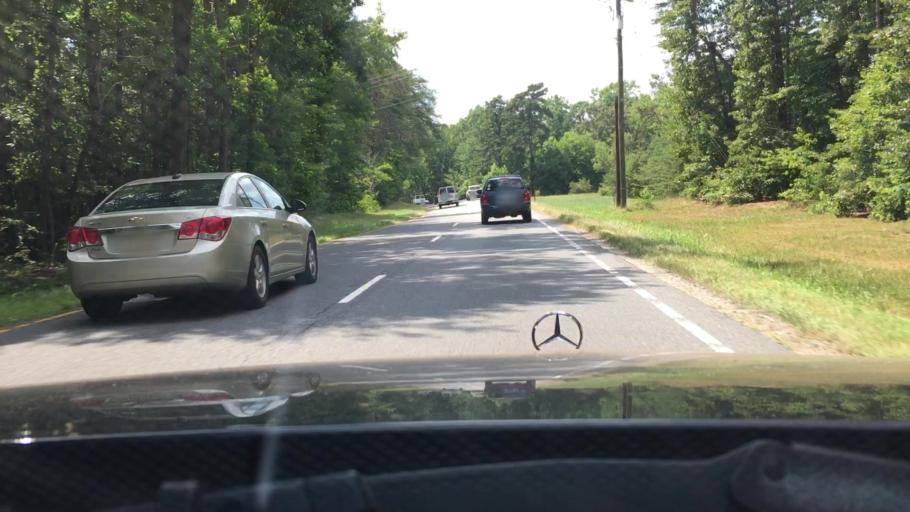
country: US
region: Virginia
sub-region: Spotsylvania County
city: Spotsylvania
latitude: 38.3056
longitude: -77.6248
